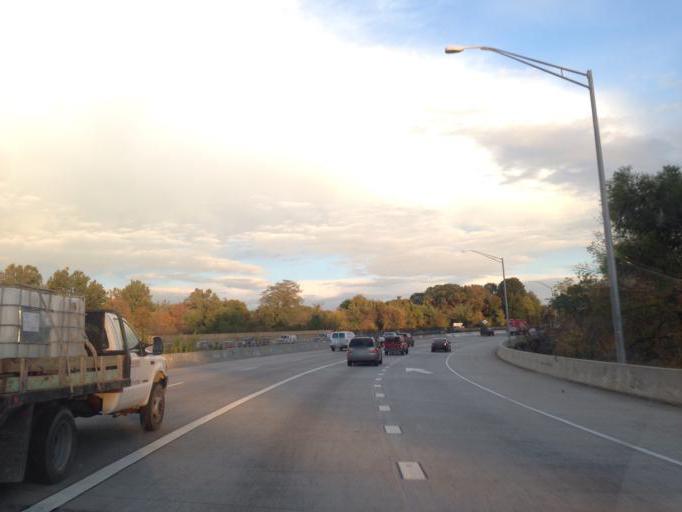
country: US
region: Maryland
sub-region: Baltimore County
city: Pikesville
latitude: 39.3756
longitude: -76.7507
